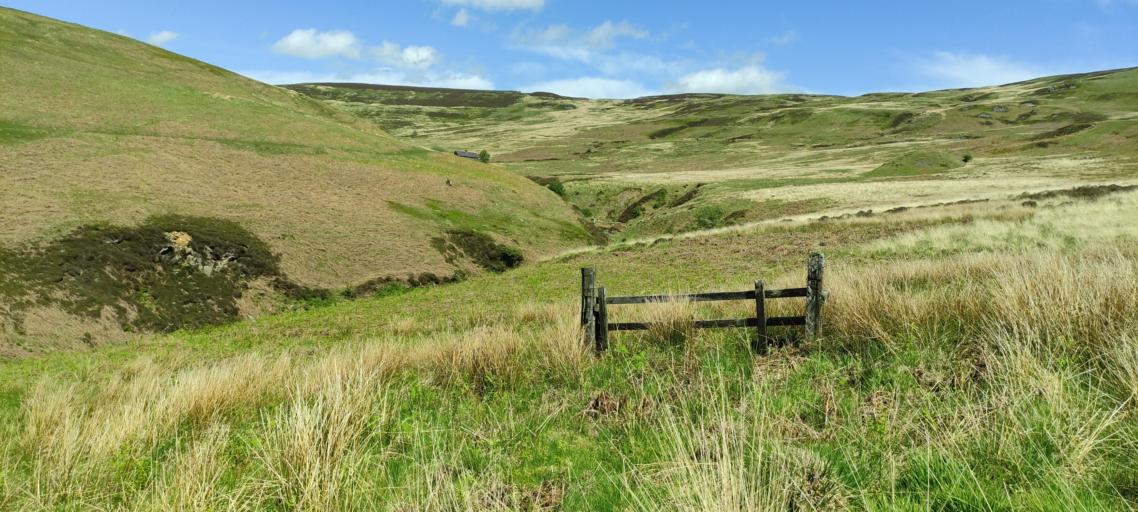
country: GB
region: England
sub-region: Cumbria
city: Brampton
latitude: 54.8896
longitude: -2.6577
